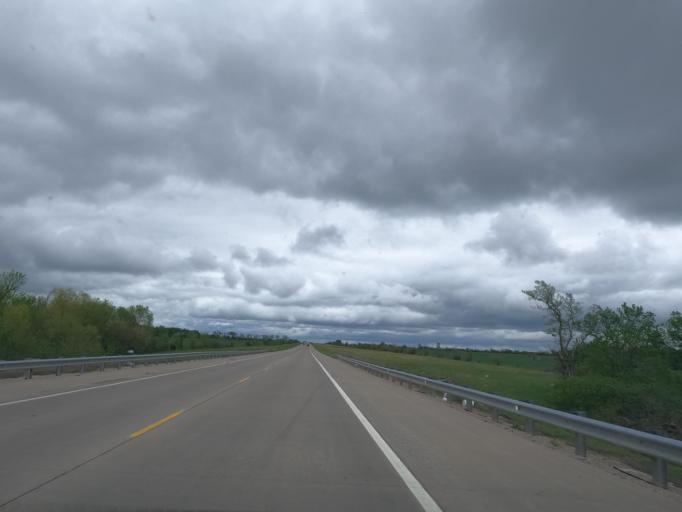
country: US
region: Kansas
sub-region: Labette County
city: Parsons
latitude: 37.3556
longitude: -95.3136
